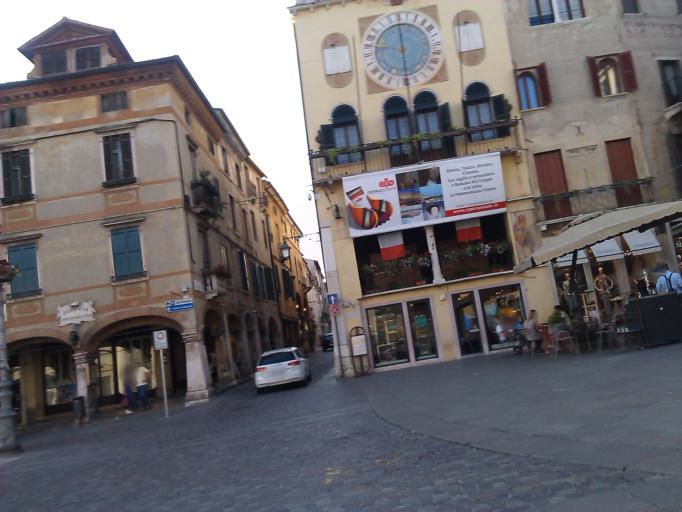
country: IT
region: Veneto
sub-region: Provincia di Vicenza
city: Bassano del Grappa
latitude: 45.7668
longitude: 11.7346
